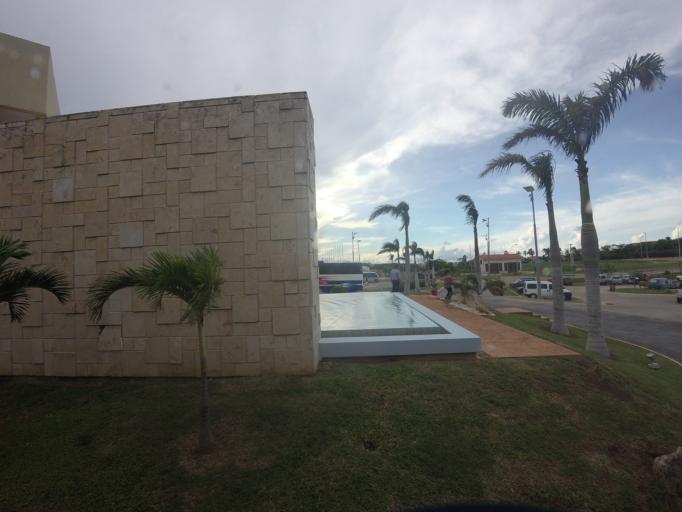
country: CU
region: Matanzas
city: Varadero
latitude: 23.1957
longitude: -81.1297
